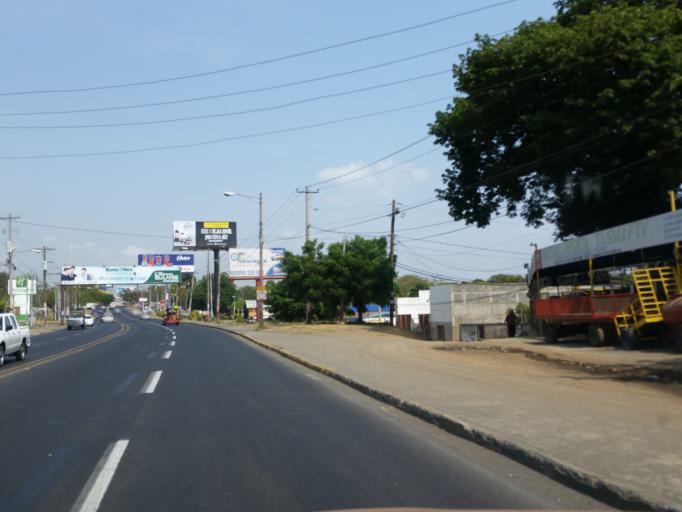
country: NI
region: Managua
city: Managua
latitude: 12.1247
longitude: -86.2784
